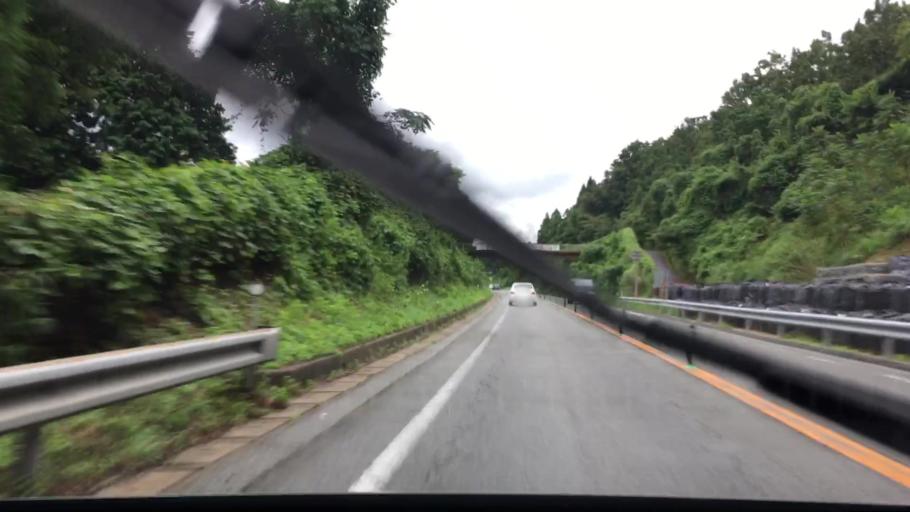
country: JP
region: Hyogo
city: Nishiwaki
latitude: 35.1035
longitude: 134.7778
